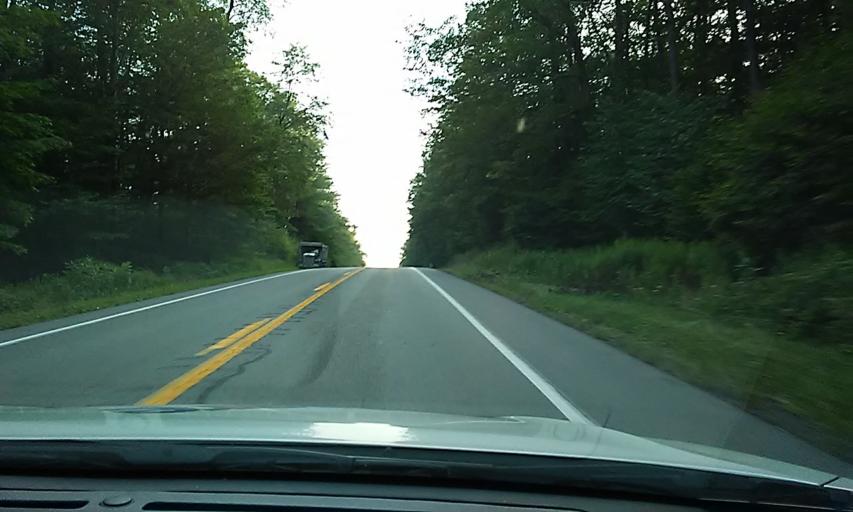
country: US
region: Pennsylvania
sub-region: Warren County
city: Sheffield
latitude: 41.5612
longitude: -78.9916
